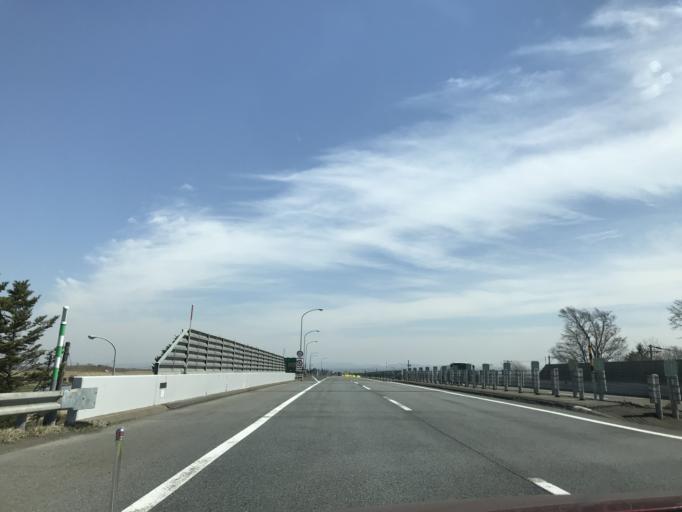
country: JP
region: Hokkaido
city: Iwamizawa
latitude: 43.1415
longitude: 141.6736
